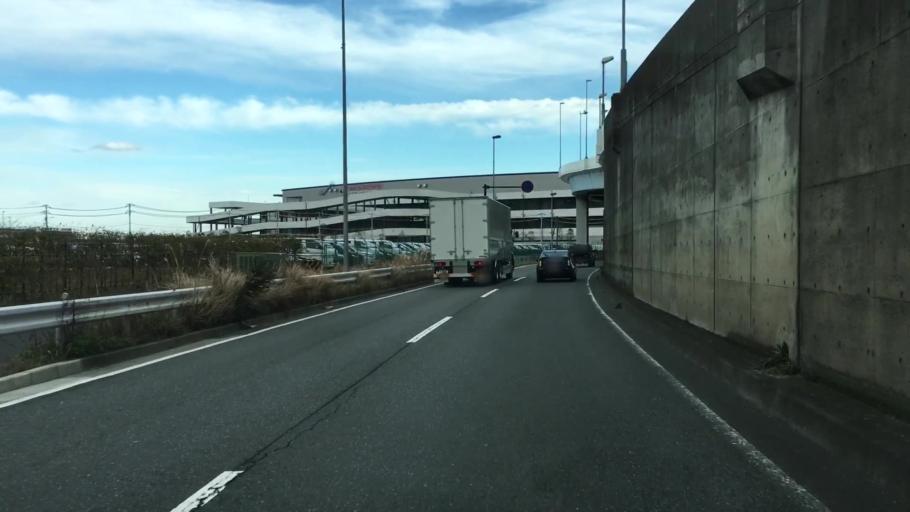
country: JP
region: Kanagawa
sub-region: Kawasaki-shi
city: Kawasaki
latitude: 35.5382
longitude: 139.7564
